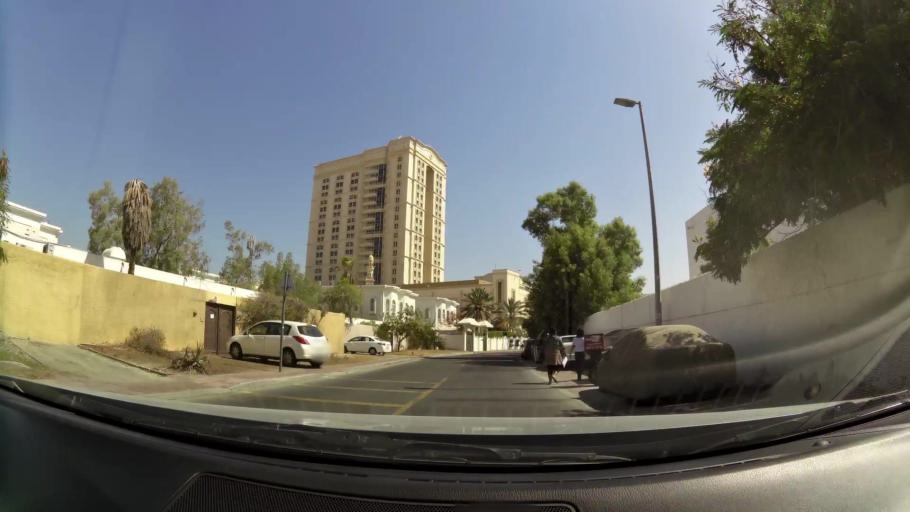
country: AE
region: Ash Shariqah
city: Sharjah
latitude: 25.2352
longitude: 55.2727
